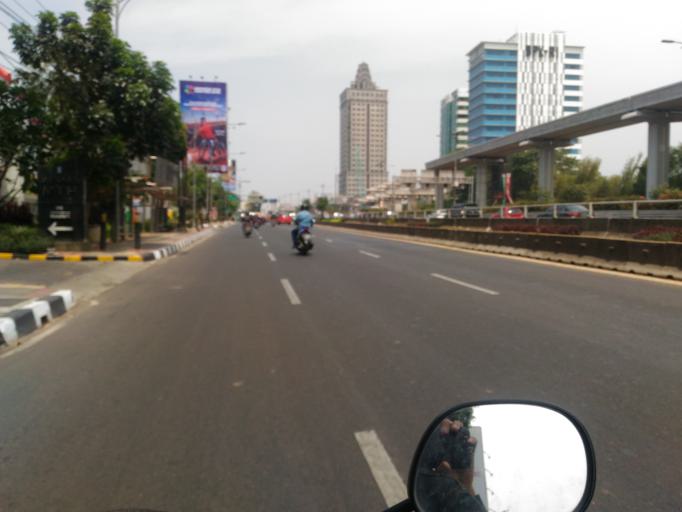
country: ID
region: Jakarta Raya
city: Jakarta
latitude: -6.2430
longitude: 106.8548
